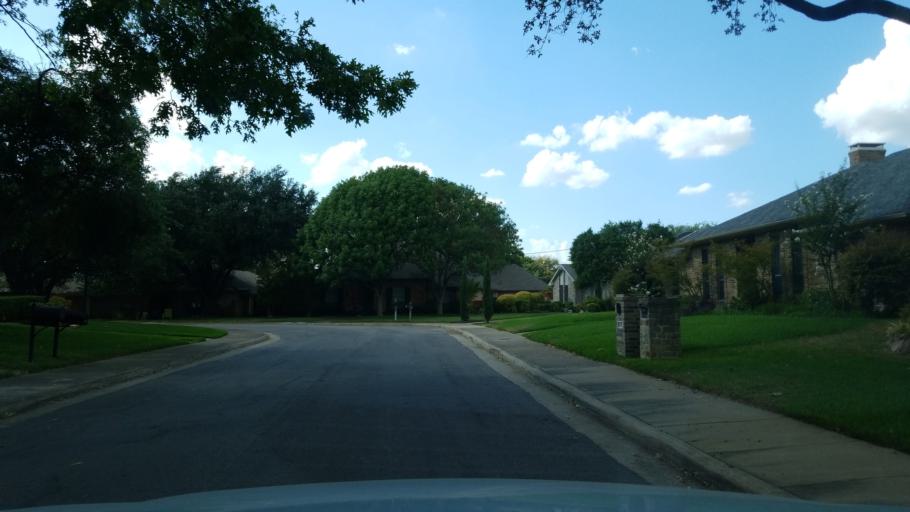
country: US
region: Texas
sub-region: Dallas County
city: Addison
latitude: 32.9696
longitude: -96.7964
